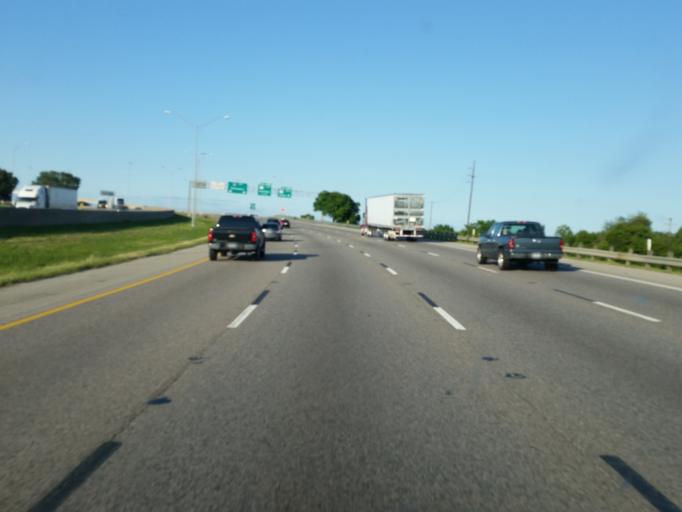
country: US
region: Texas
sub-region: Dallas County
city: Balch Springs
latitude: 32.6870
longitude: -96.6374
